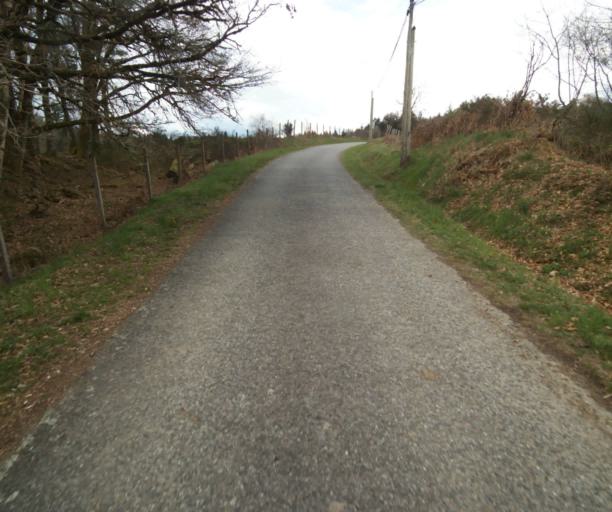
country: FR
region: Limousin
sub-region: Departement de la Correze
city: Correze
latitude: 45.2862
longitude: 1.9307
